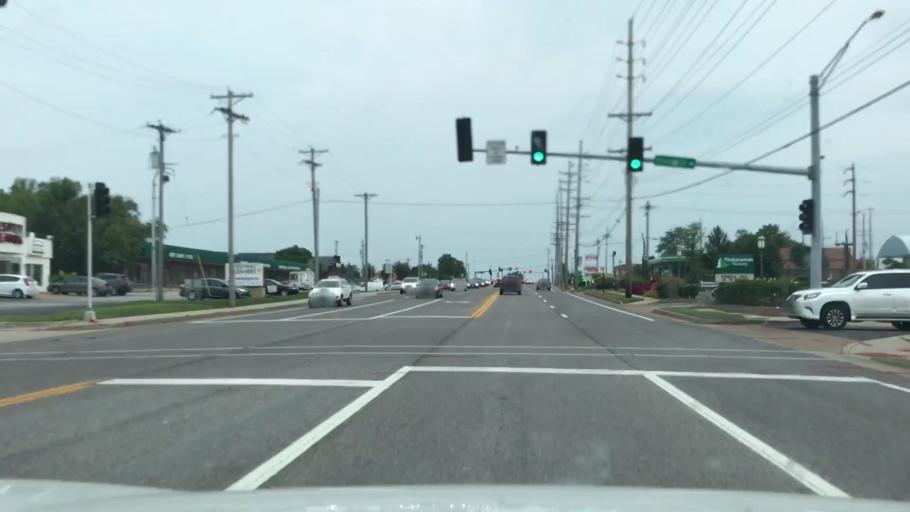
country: US
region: Missouri
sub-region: Saint Louis County
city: Ellisville
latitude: 38.5957
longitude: -90.5858
